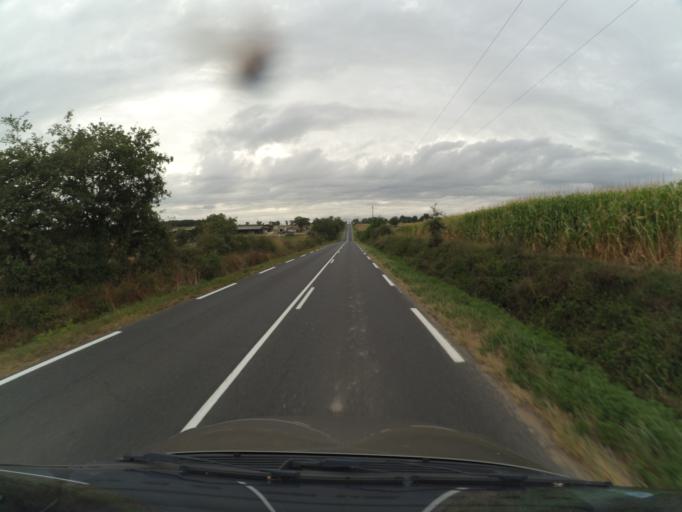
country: FR
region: Pays de la Loire
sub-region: Departement de Maine-et-Loire
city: Le Longeron
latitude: 47.0298
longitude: -1.0832
